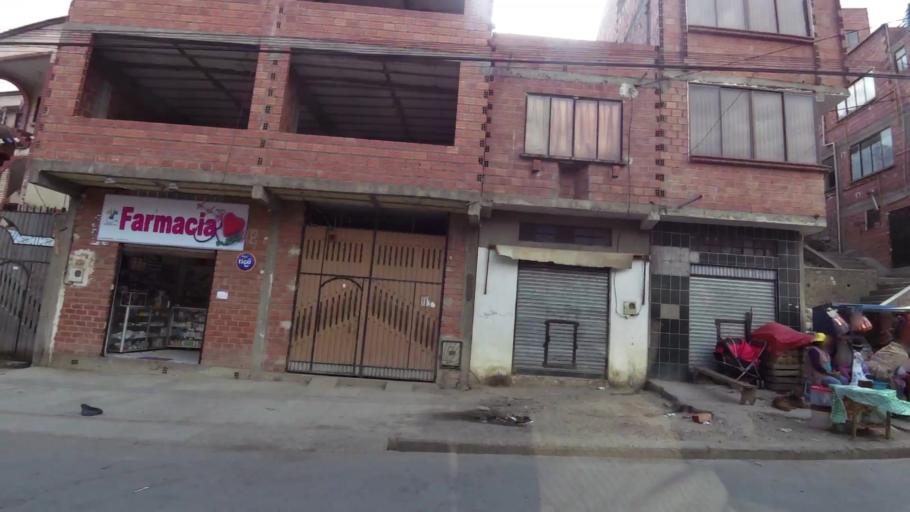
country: BO
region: La Paz
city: La Paz
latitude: -16.4596
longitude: -68.1029
